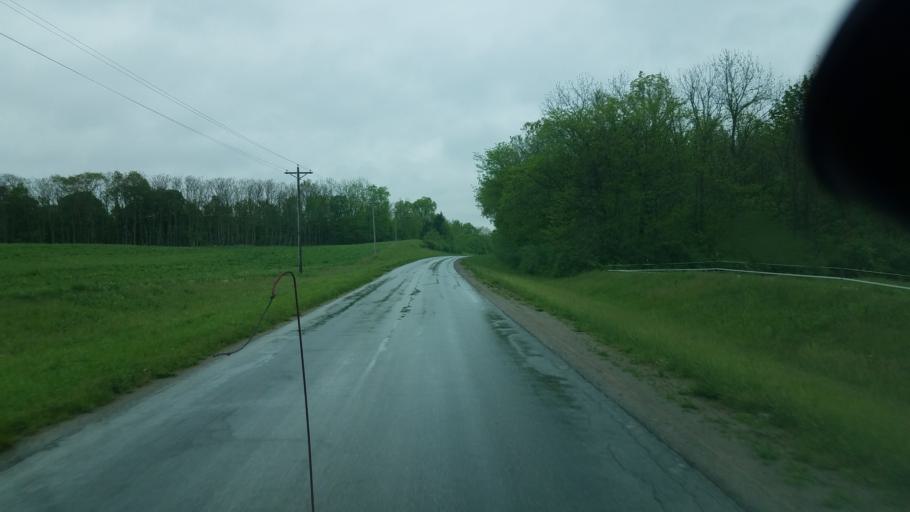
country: US
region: Ohio
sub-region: Highland County
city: Greenfield
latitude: 39.2879
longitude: -83.4587
